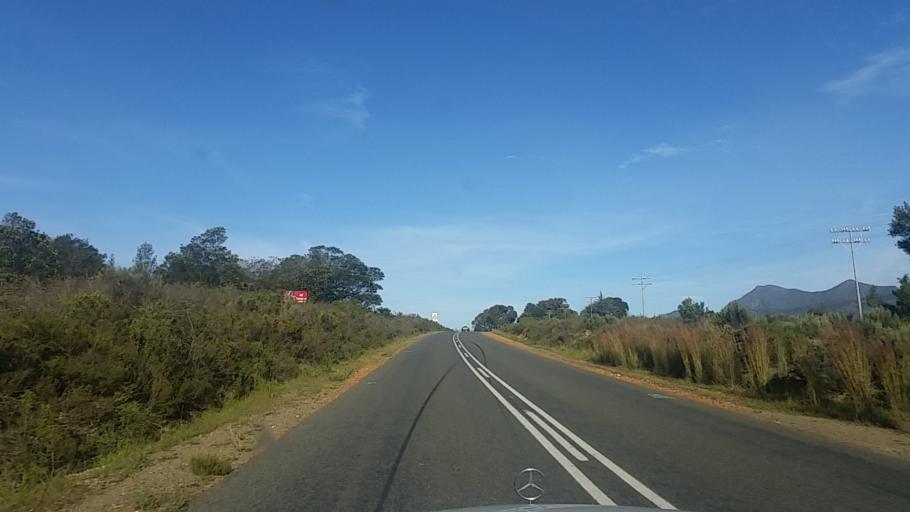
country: ZA
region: Western Cape
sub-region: Eden District Municipality
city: Knysna
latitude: -33.7612
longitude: 22.8791
